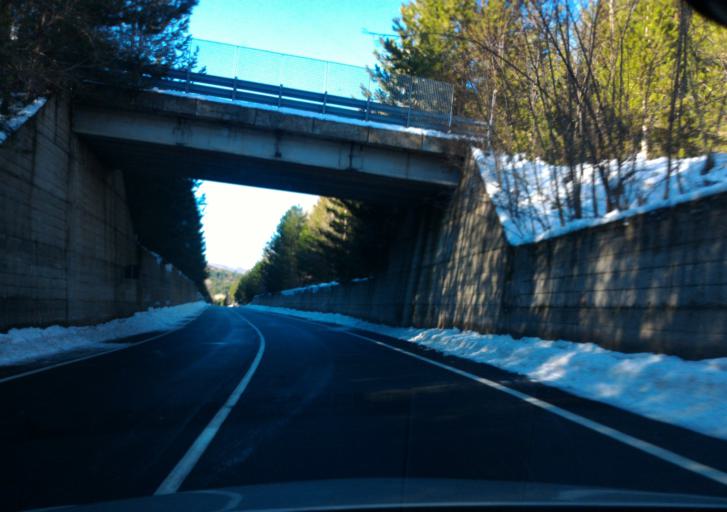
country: IT
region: Calabria
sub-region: Provincia di Cosenza
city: Celico
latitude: 39.3344
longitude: 16.4757
